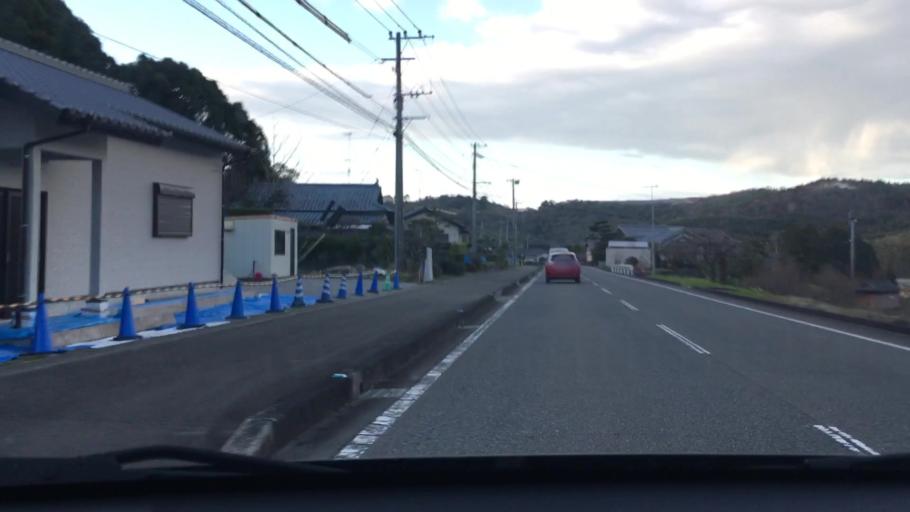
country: JP
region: Oita
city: Bungo-Takada-shi
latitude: 33.4986
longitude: 131.3762
